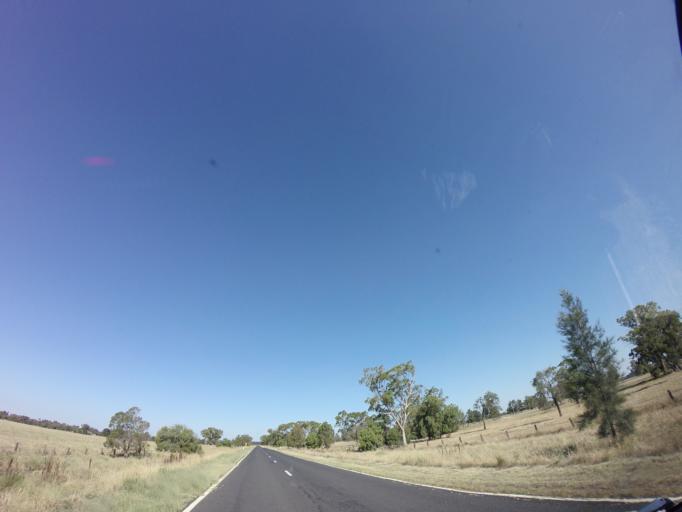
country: AU
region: New South Wales
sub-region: Gilgandra
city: Gilgandra
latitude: -31.6732
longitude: 148.2430
